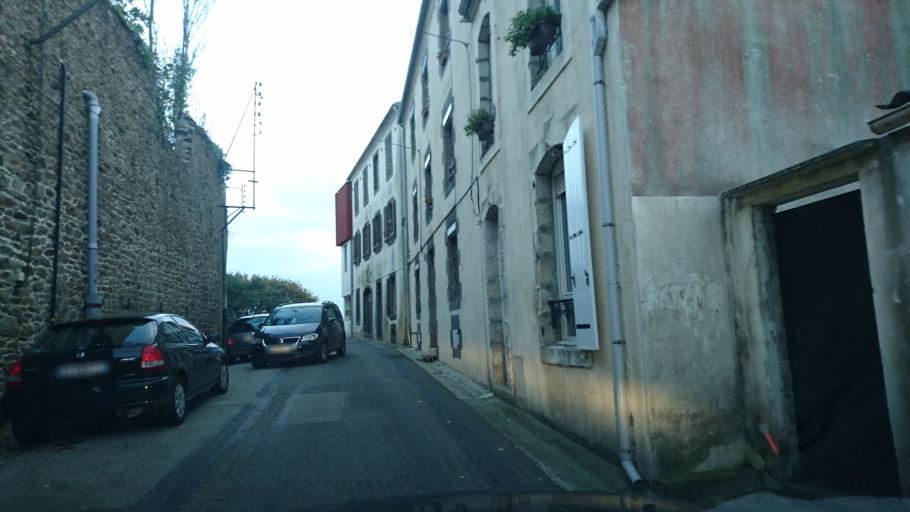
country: FR
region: Brittany
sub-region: Departement du Finistere
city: Brest
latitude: 48.3913
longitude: -4.4694
